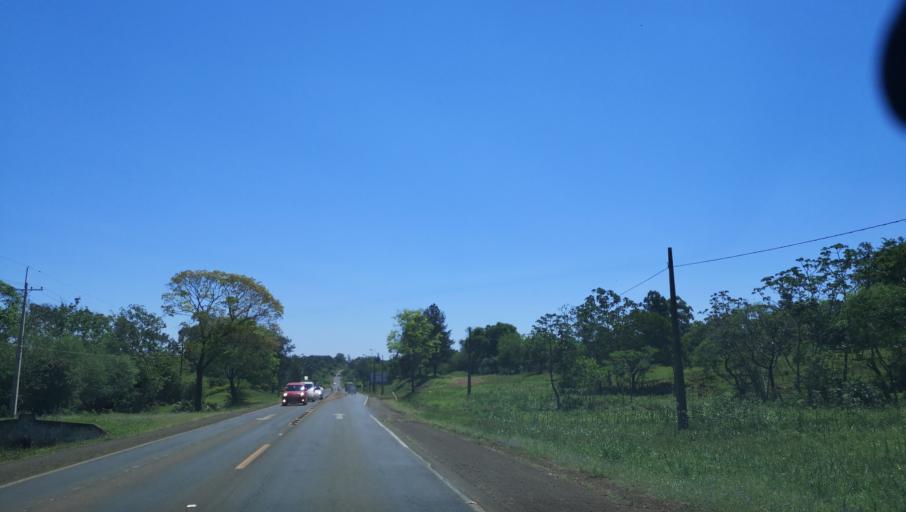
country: PY
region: Itapua
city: San Juan del Parana
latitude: -27.2573
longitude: -55.9830
